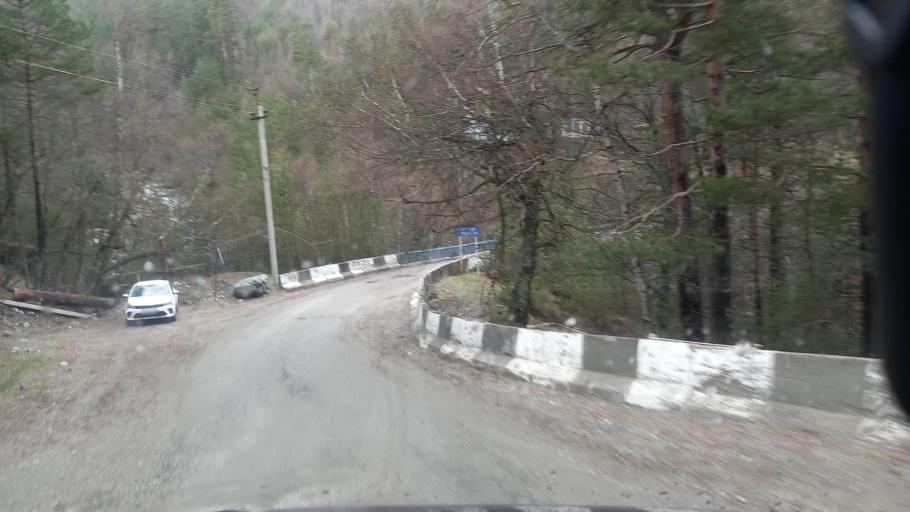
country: RU
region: Kabardino-Balkariya
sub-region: El'brusskiy Rayon
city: El'brus
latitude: 43.2290
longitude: 42.6557
